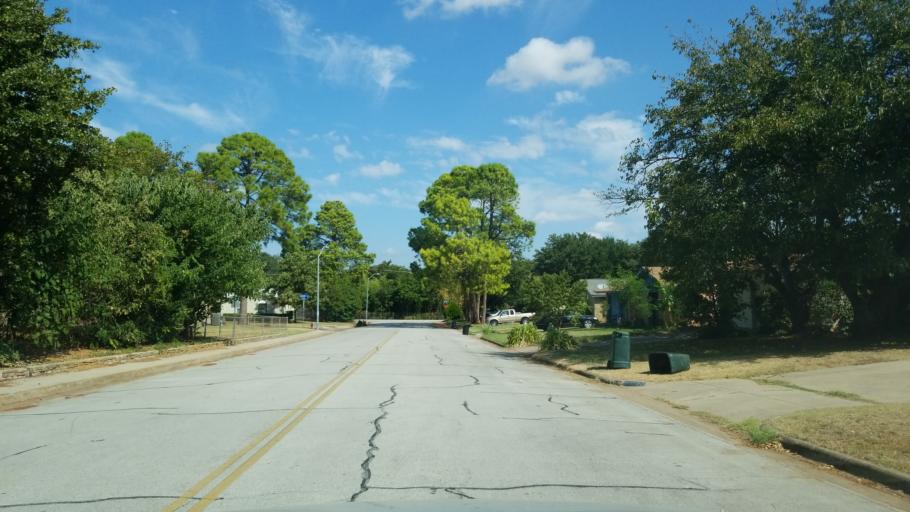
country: US
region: Texas
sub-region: Tarrant County
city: Euless
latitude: 32.8579
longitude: -97.0903
